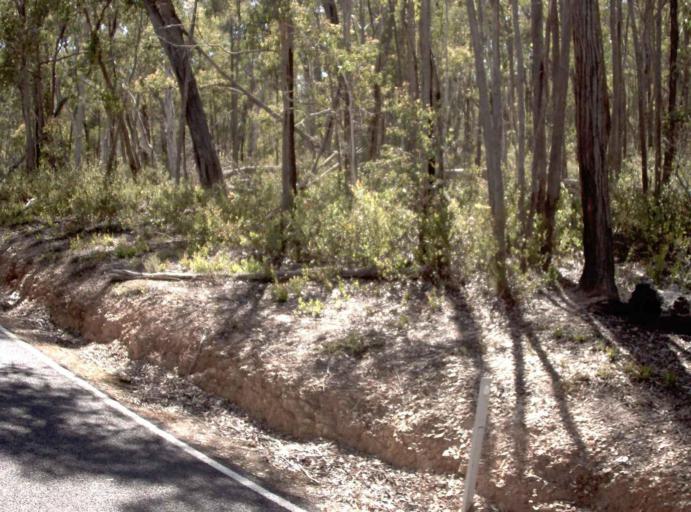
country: AU
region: New South Wales
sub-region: Bombala
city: Bombala
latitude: -37.1393
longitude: 148.7323
